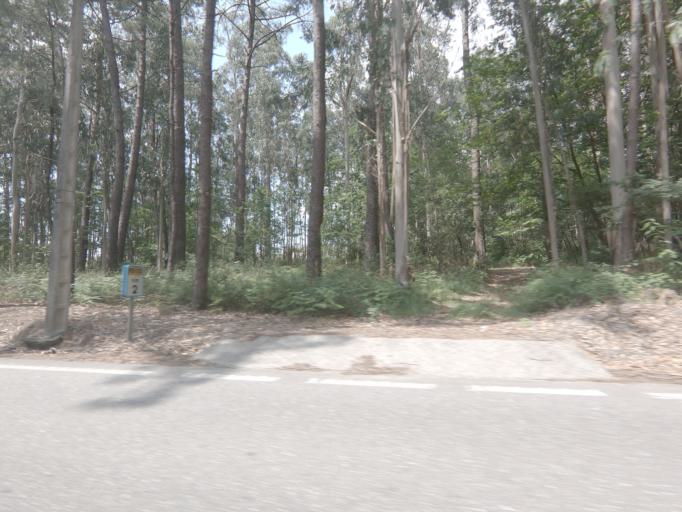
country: PT
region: Viana do Castelo
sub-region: Valenca
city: Valenca
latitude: 42.0249
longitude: -8.6806
